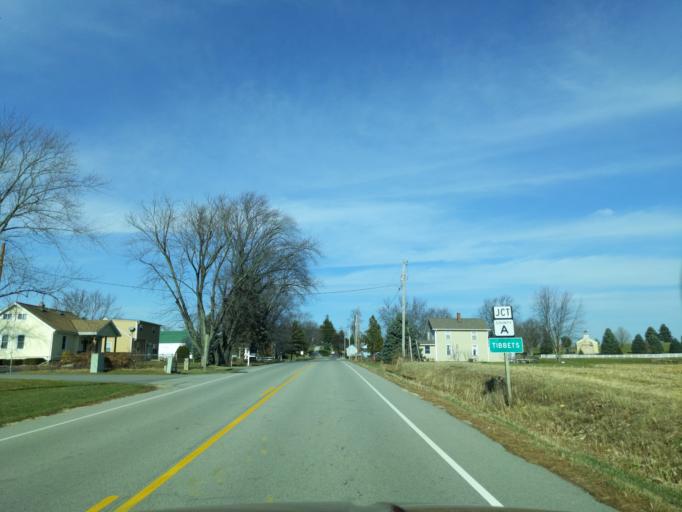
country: US
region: Wisconsin
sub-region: Walworth County
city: Elkhorn
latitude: 42.7323
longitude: -88.5822
